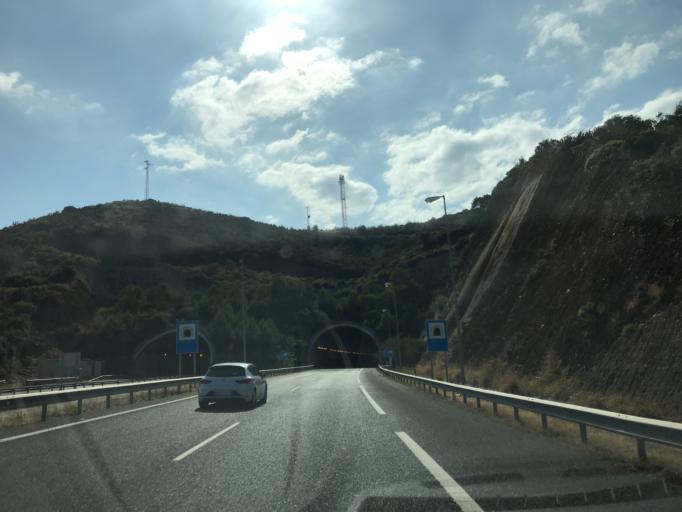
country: ES
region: Andalusia
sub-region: Provincia de Malaga
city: Istan
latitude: 36.5258
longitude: -4.9587
